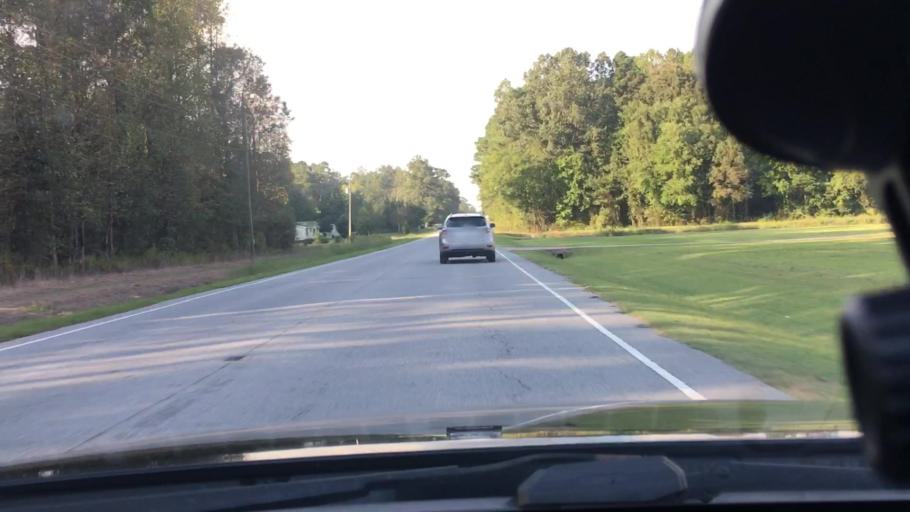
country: US
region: North Carolina
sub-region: Pitt County
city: Windsor
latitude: 35.4437
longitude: -77.2634
